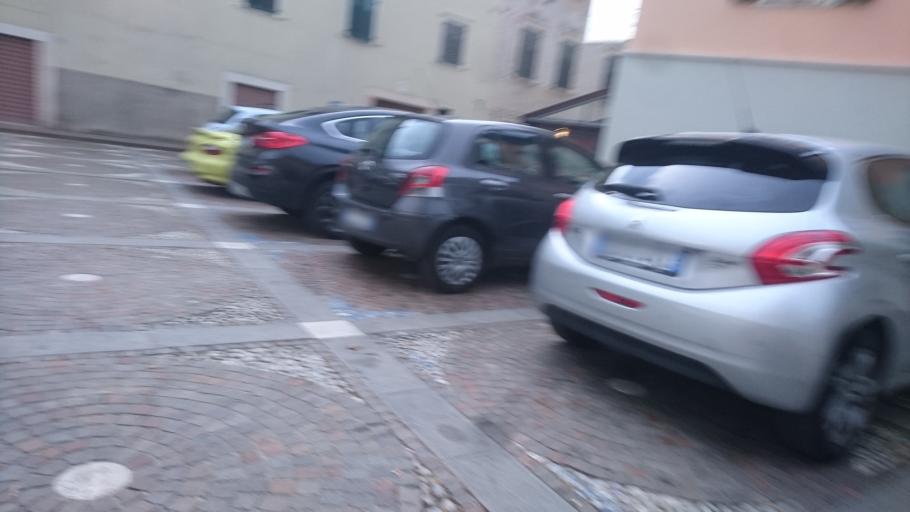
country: IT
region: Trentino-Alto Adige
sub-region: Provincia di Trento
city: Villa Lagarina
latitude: 45.9168
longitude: 11.0306
